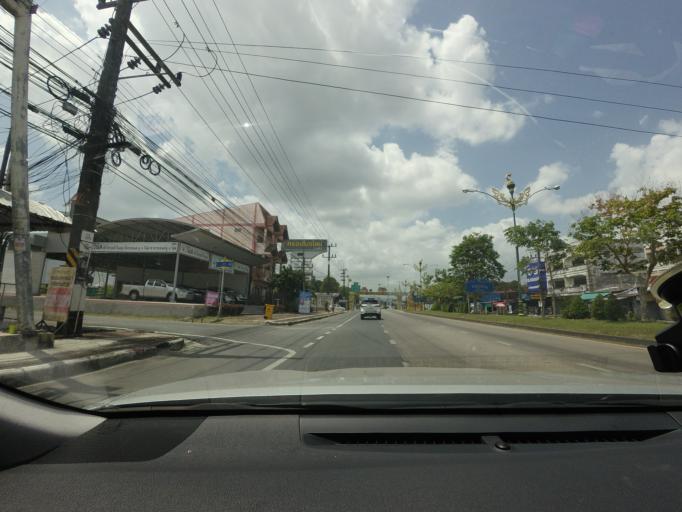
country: TH
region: Nakhon Si Thammarat
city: Nakhon Si Thammarat
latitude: 8.4340
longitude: 99.9237
